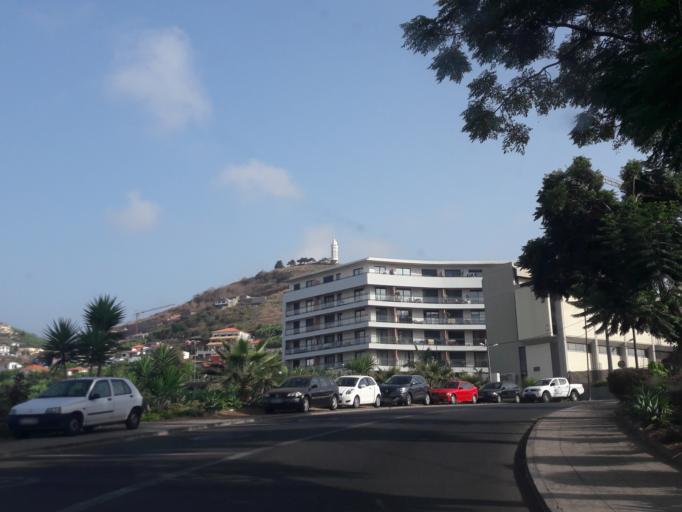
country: PT
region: Madeira
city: Camara de Lobos
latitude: 32.6437
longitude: -16.9444
